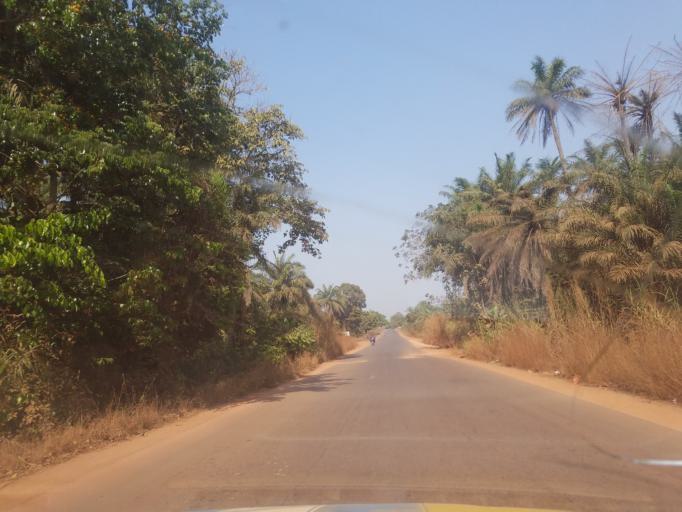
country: GN
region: Boke
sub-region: Boke Prefecture
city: Sangueya
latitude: 10.8276
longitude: -14.3694
